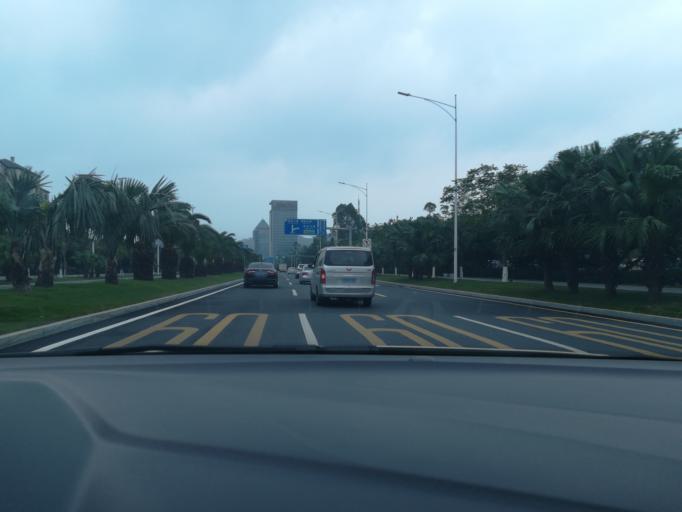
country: CN
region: Guangdong
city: Nansha
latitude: 22.7787
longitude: 113.5958
